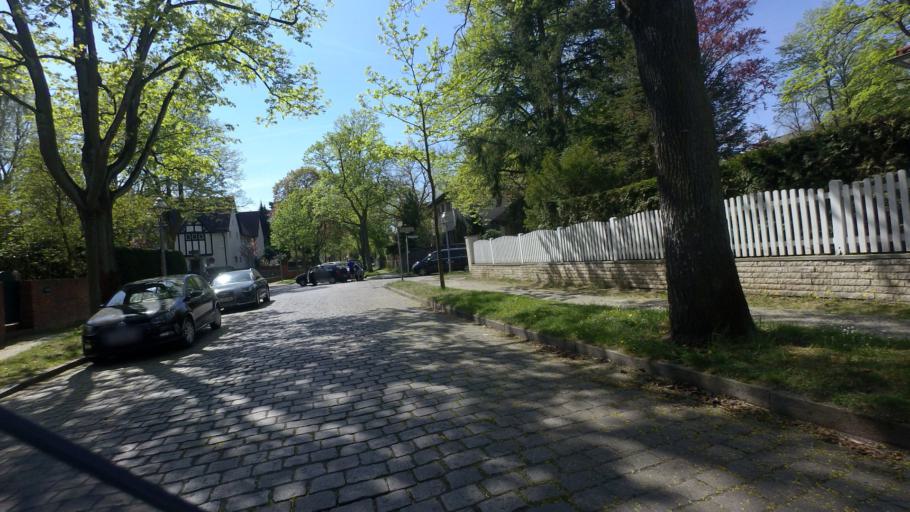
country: DE
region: Berlin
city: Zehlendorf Bezirk
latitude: 52.4442
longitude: 13.2316
